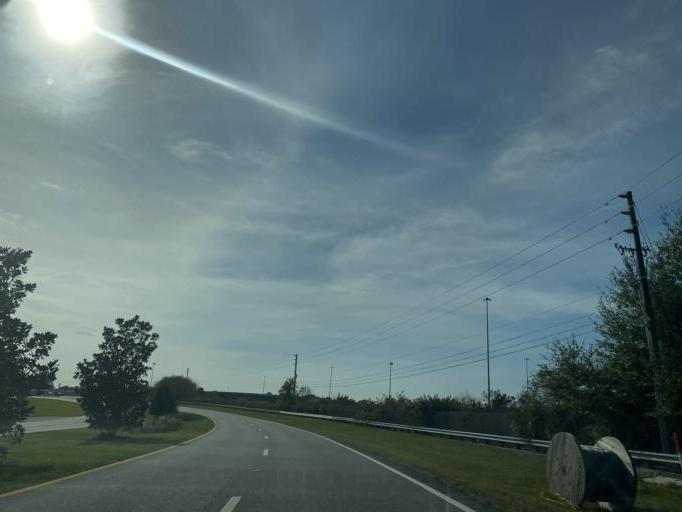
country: US
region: Florida
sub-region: Seminole County
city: Heathrow
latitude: 28.7911
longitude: -81.3461
